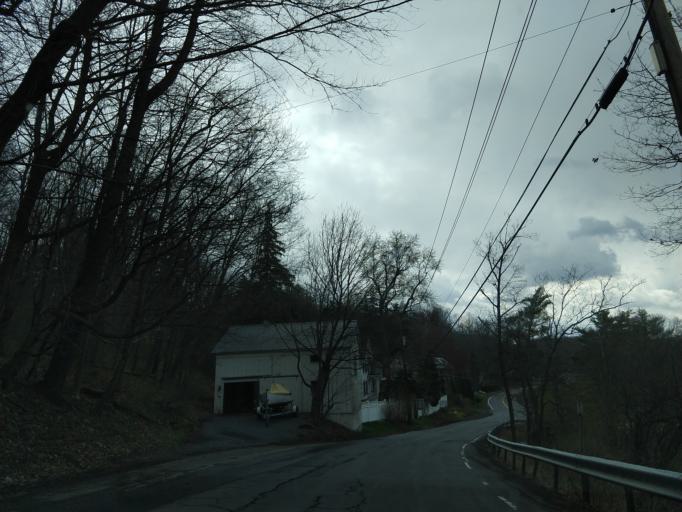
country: US
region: New York
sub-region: Tompkins County
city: East Ithaca
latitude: 42.4539
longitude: -76.4710
